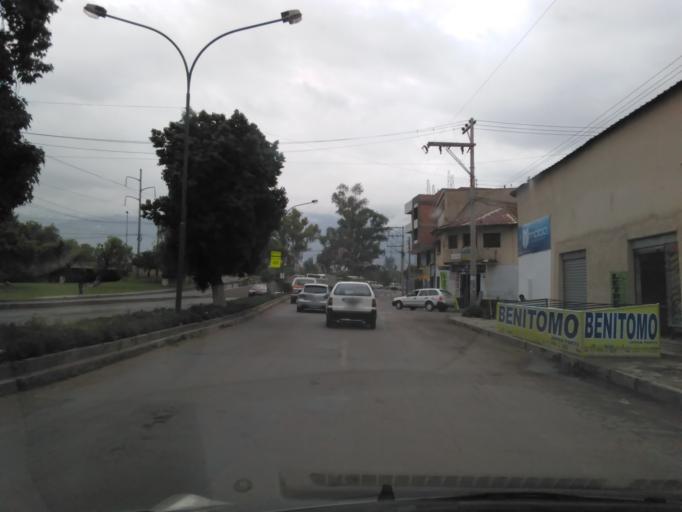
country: BO
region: Cochabamba
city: Cochabamba
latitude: -17.3951
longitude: -66.1668
